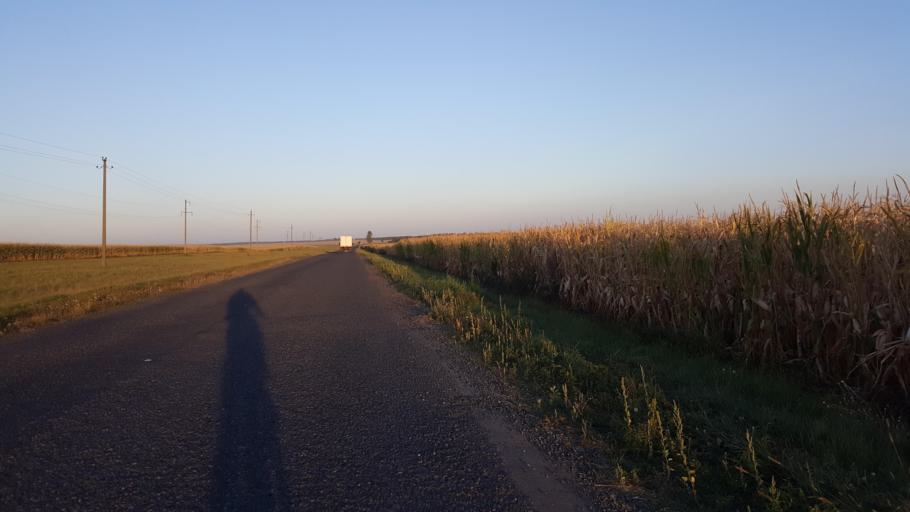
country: BY
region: Brest
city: Charnawchytsy
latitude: 52.2913
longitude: 23.5638
